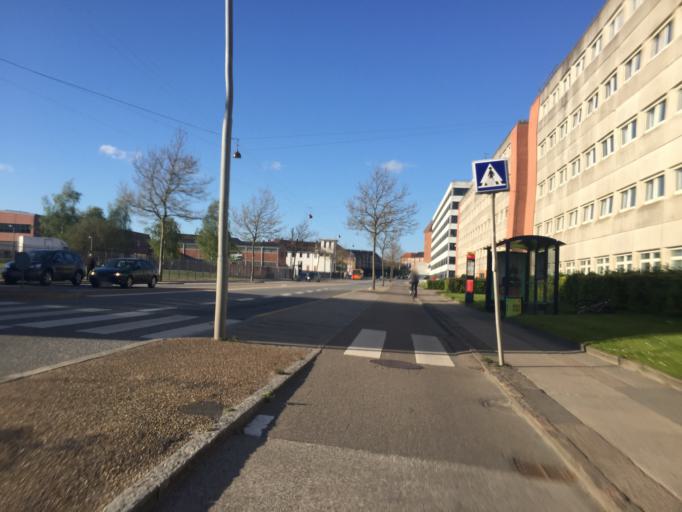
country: DK
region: Capital Region
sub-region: Frederiksberg Kommune
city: Frederiksberg
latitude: 55.6585
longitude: 12.5144
